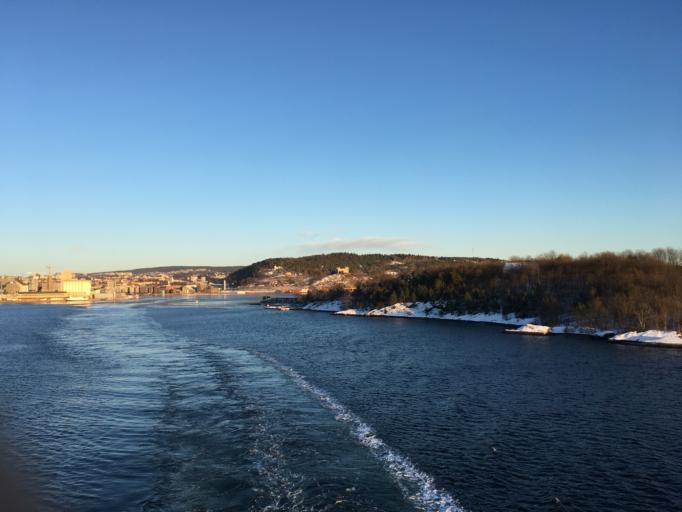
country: NO
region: Oslo
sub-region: Oslo
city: Oslo
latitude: 59.8988
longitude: 10.7214
